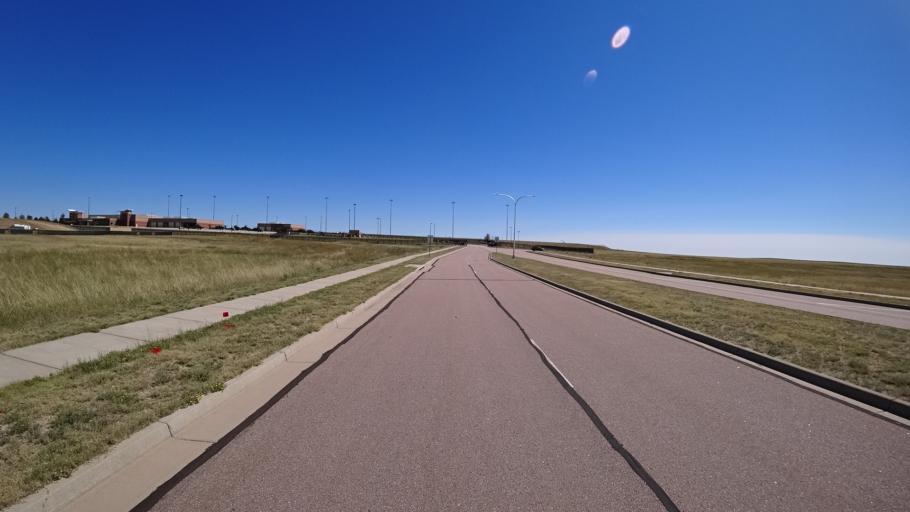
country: US
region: Colorado
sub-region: El Paso County
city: Security-Widefield
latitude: 38.7759
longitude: -104.6974
